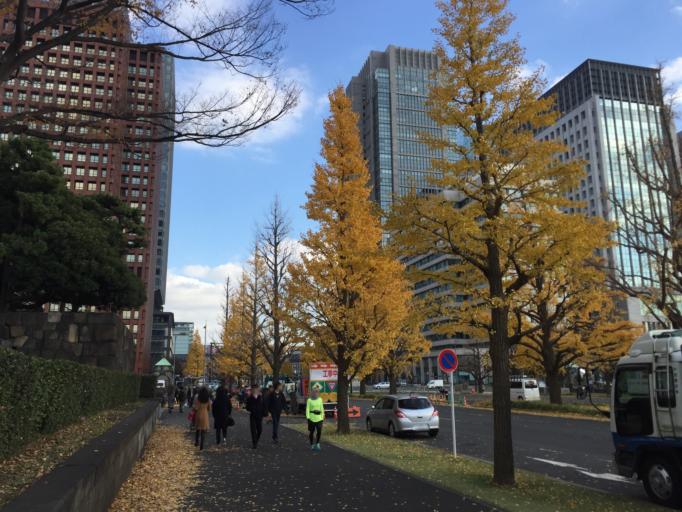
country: JP
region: Tokyo
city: Tokyo
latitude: 35.6829
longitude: 139.7609
